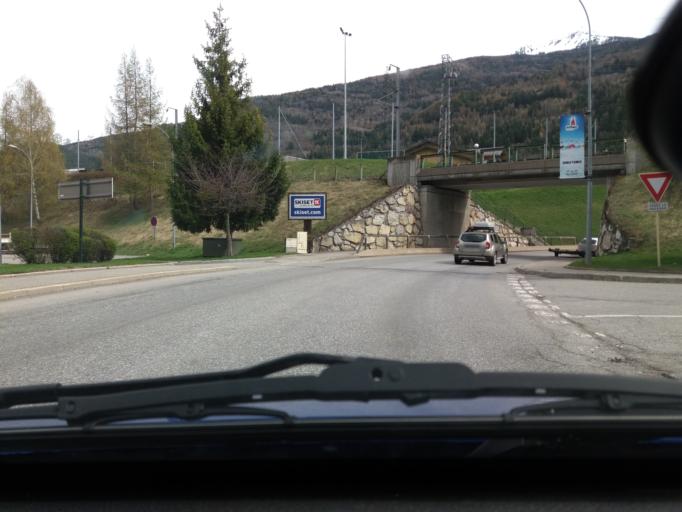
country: FR
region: Rhone-Alpes
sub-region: Departement de la Savoie
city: Macot-la-Plagne
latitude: 45.5557
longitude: 6.6612
